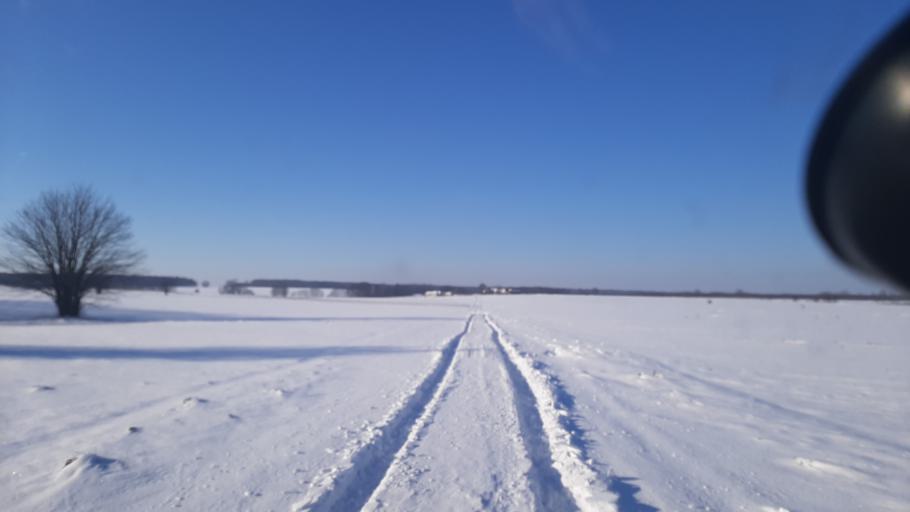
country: PL
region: Lublin Voivodeship
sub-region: Powiat lubelski
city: Jastkow
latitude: 51.3794
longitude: 22.4318
